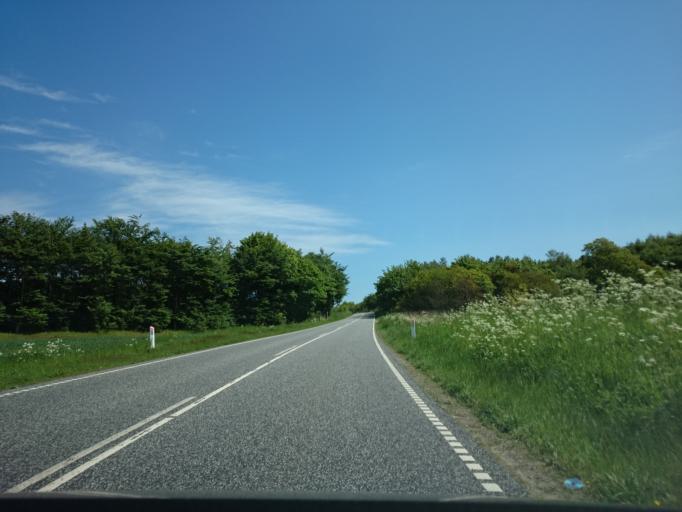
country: DK
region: Central Jutland
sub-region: Randers Kommune
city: Assentoft
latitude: 56.4082
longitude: 10.1244
